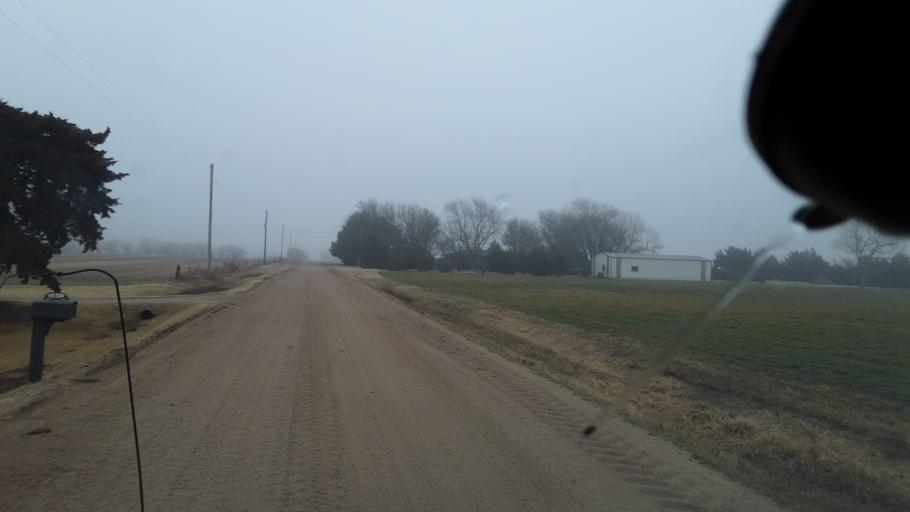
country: US
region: Kansas
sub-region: Reno County
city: South Hutchinson
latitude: 37.9845
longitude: -98.0046
